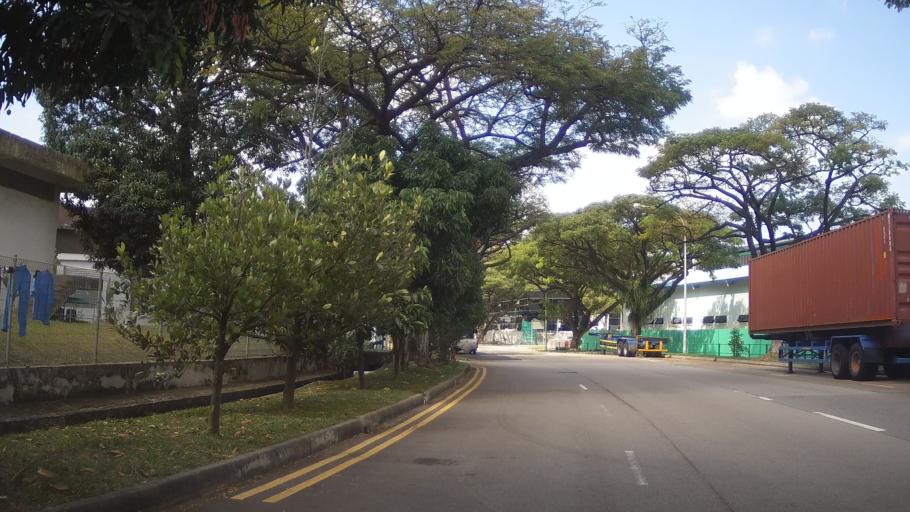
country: MY
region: Johor
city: Johor Bahru
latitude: 1.3167
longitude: 103.6652
